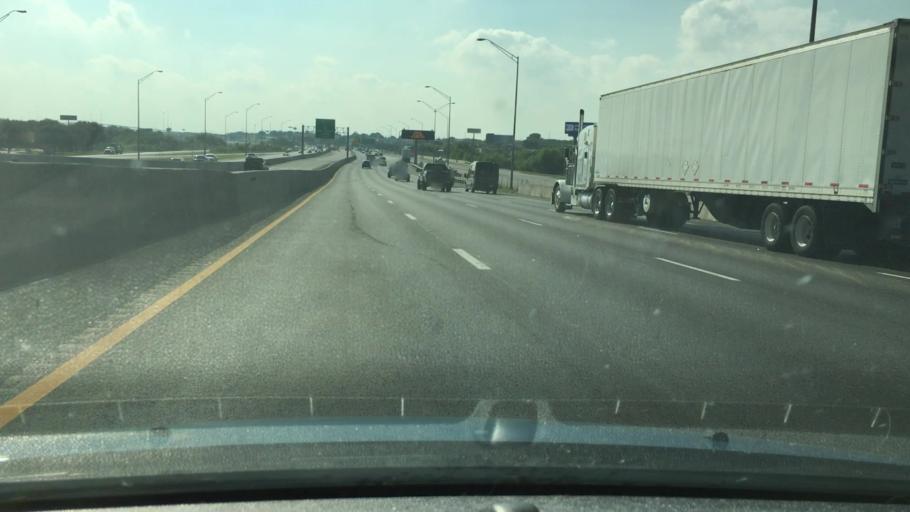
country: US
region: Texas
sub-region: Denton County
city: Lewisville
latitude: 33.0176
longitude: -96.9829
